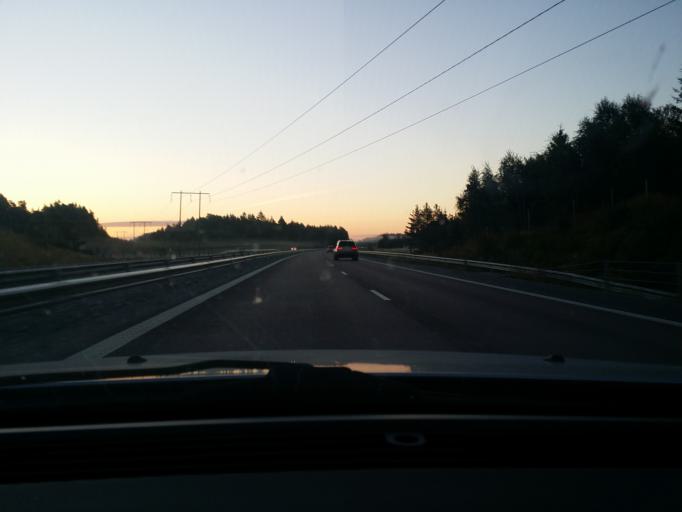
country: SE
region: Vaestmanland
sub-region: Vasteras
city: Tillberga
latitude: 59.6247
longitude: 16.7653
